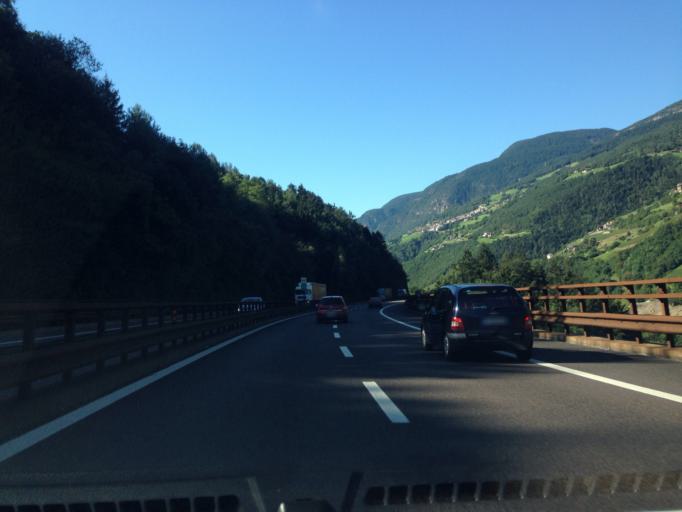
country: IT
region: Trentino-Alto Adige
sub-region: Bolzano
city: Villandro
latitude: 46.6254
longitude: 11.5498
